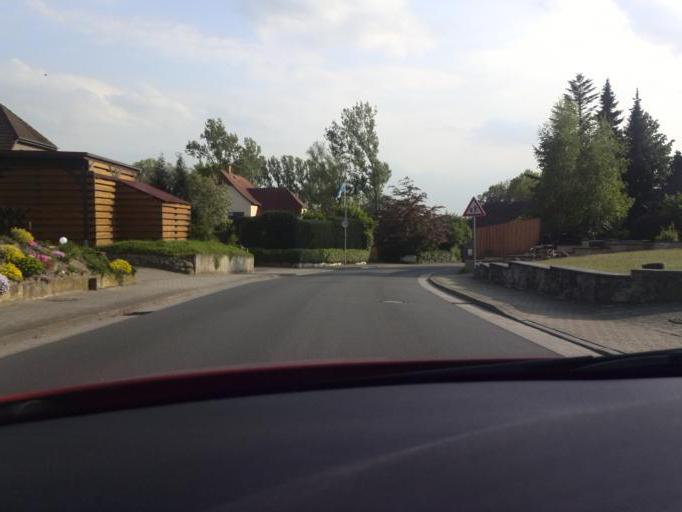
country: DE
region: Lower Saxony
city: Calberlah
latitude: 52.3970
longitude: 10.6515
